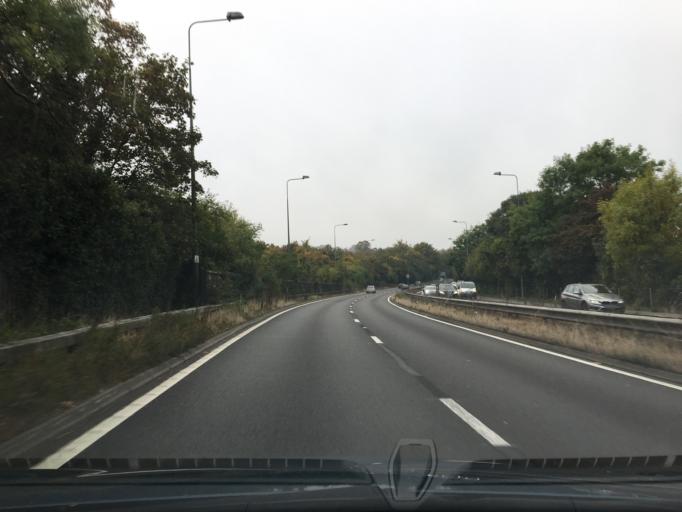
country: GB
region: England
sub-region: Surrey
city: Guildford
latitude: 51.2349
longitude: -0.6026
